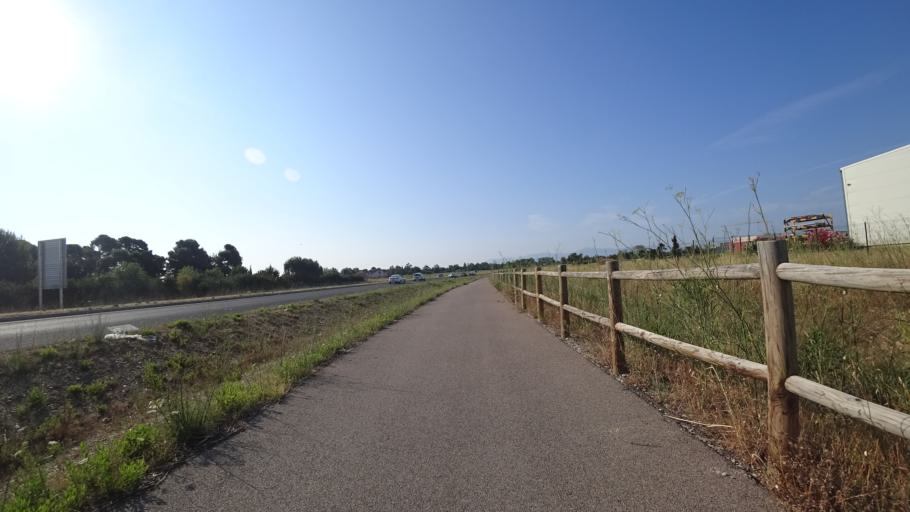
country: FR
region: Languedoc-Roussillon
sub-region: Departement des Pyrenees-Orientales
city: Pia
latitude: 42.7256
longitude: 2.9014
